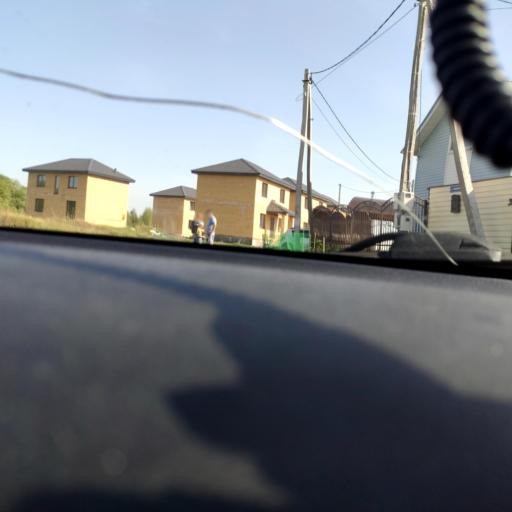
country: RU
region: Tatarstan
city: Stolbishchi
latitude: 55.7210
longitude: 49.3383
